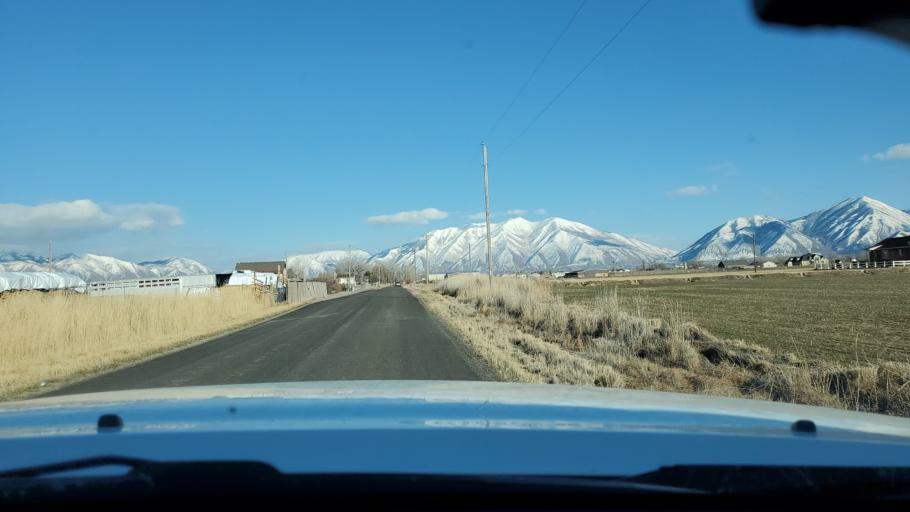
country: US
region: Utah
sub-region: Utah County
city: Benjamin
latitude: 40.1144
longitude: -111.7579
